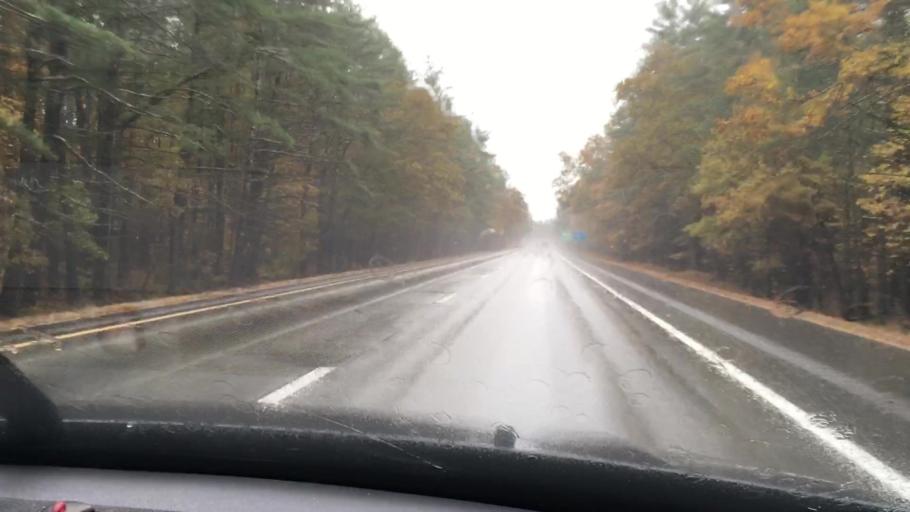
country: US
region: New Hampshire
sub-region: Merrimack County
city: Canterbury
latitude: 43.3032
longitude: -71.5827
